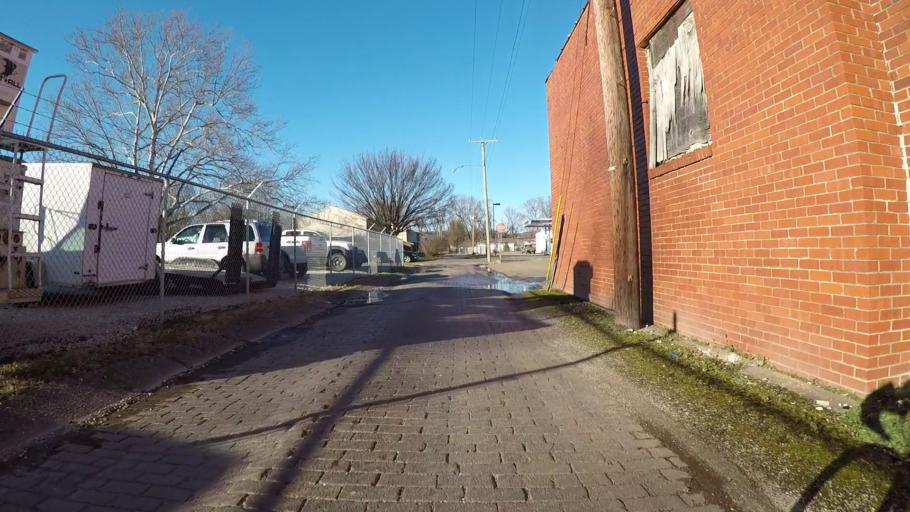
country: US
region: West Virginia
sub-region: Cabell County
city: Huntington
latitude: 38.4290
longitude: -82.3834
